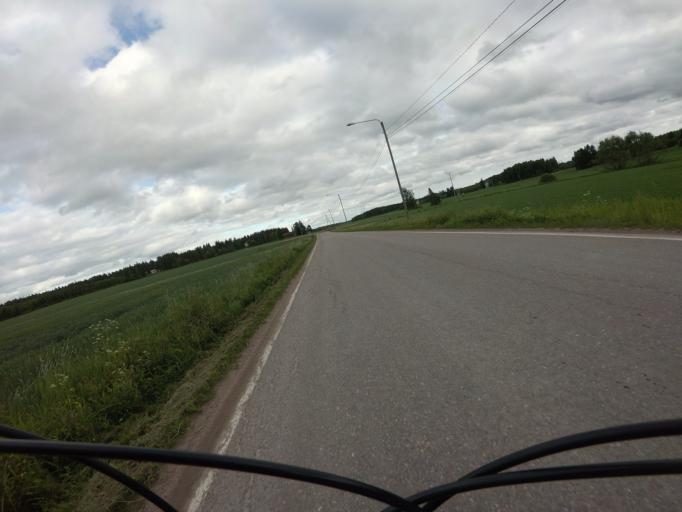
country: FI
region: Varsinais-Suomi
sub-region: Turku
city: Lieto
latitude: 60.5365
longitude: 22.3887
